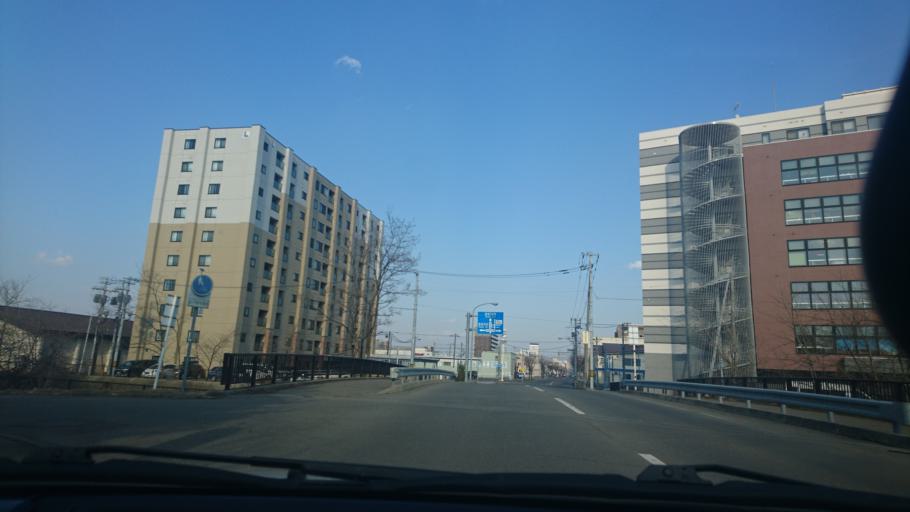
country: JP
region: Hokkaido
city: Obihiro
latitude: 42.9252
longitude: 143.1923
